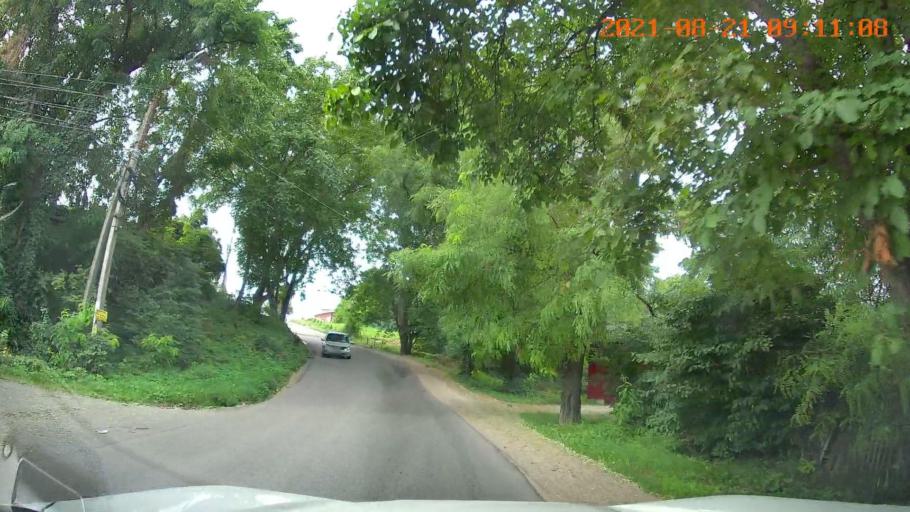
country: RU
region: Stavropol'skiy
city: Goryachevodskiy
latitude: 44.0193
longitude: 43.0719
